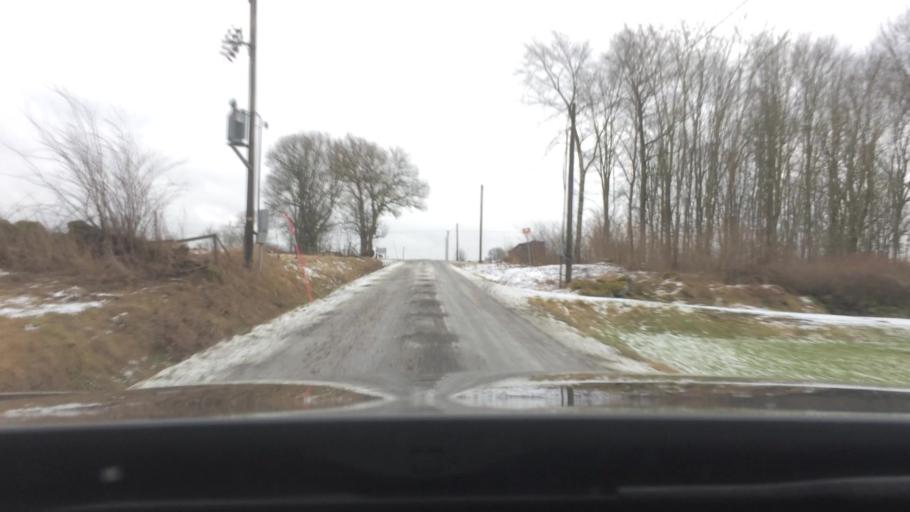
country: SE
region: Vaestra Goetaland
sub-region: Falkopings Kommun
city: Floby
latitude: 57.9947
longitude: 13.3974
